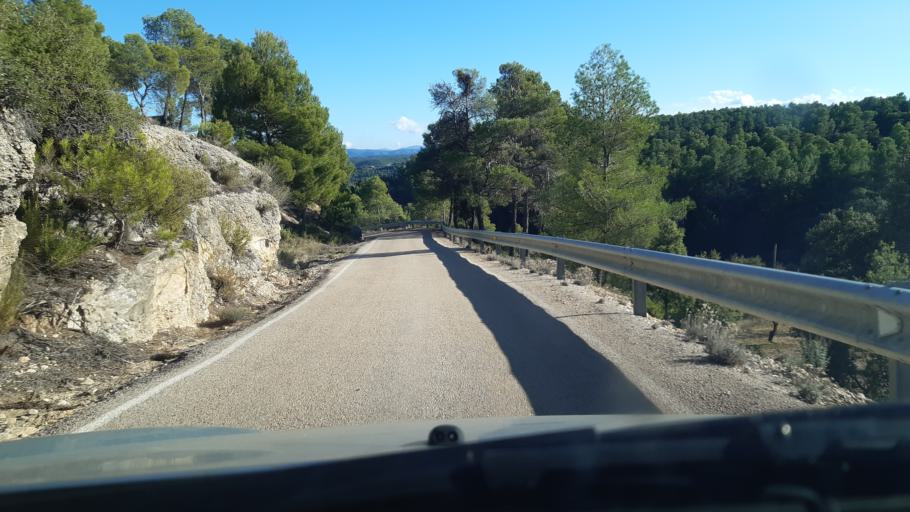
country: ES
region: Aragon
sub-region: Provincia de Teruel
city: Fornoles
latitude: 40.9110
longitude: -0.0175
